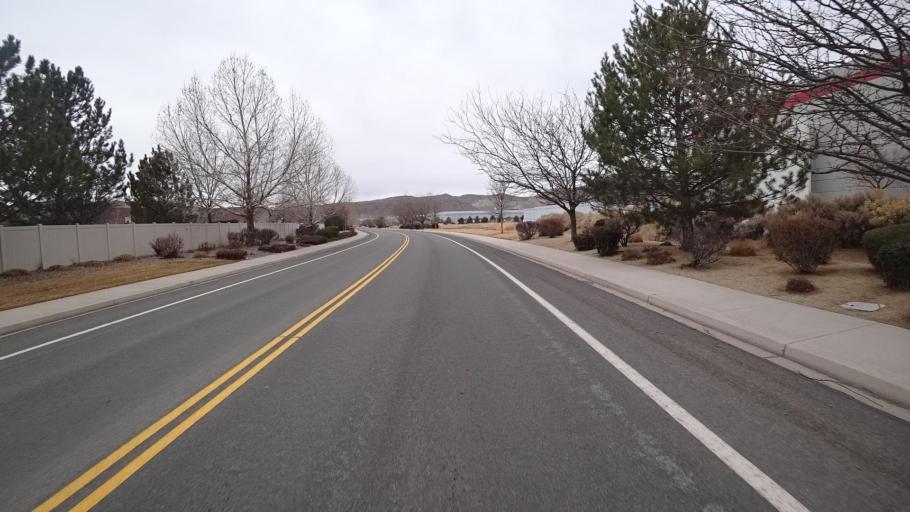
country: US
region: Nevada
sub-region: Washoe County
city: Spanish Springs
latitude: 39.6712
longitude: -119.7088
